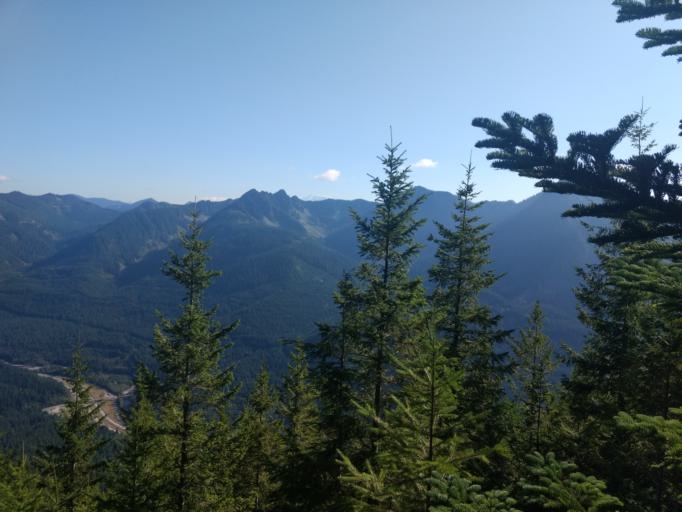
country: US
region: Washington
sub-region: King County
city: Tanner
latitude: 47.4351
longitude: -121.5909
